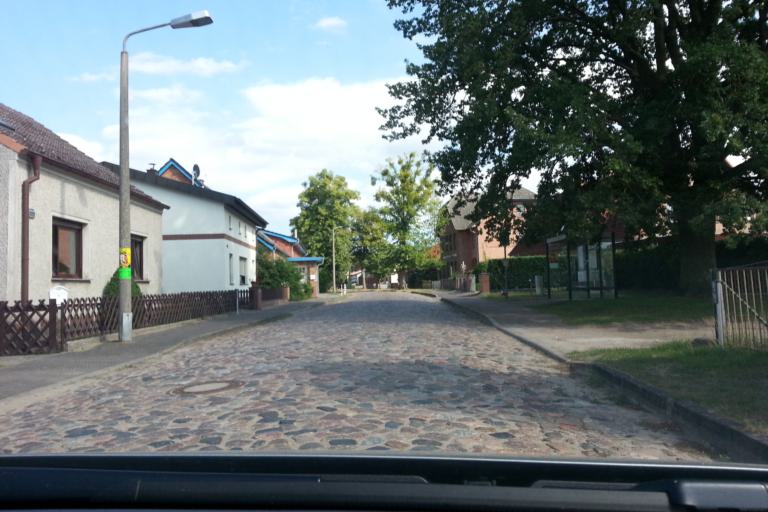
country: DE
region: Mecklenburg-Vorpommern
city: Ferdinandshof
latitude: 53.6302
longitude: 13.8608
